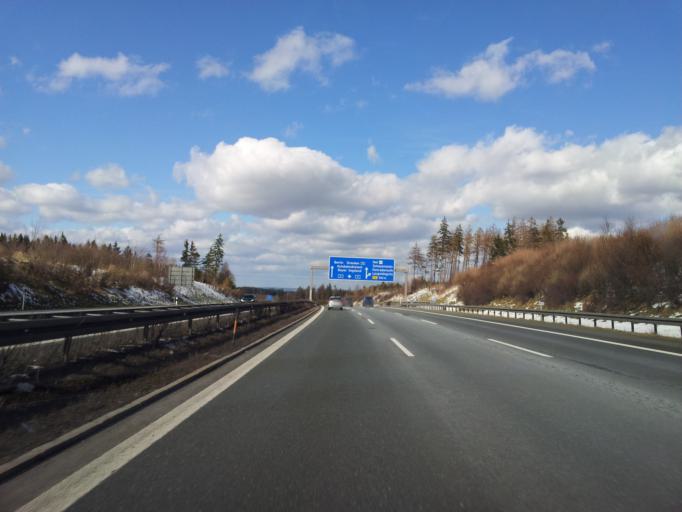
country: DE
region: Bavaria
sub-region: Upper Franconia
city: Leupoldsgrun
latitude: 50.2823
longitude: 11.8116
